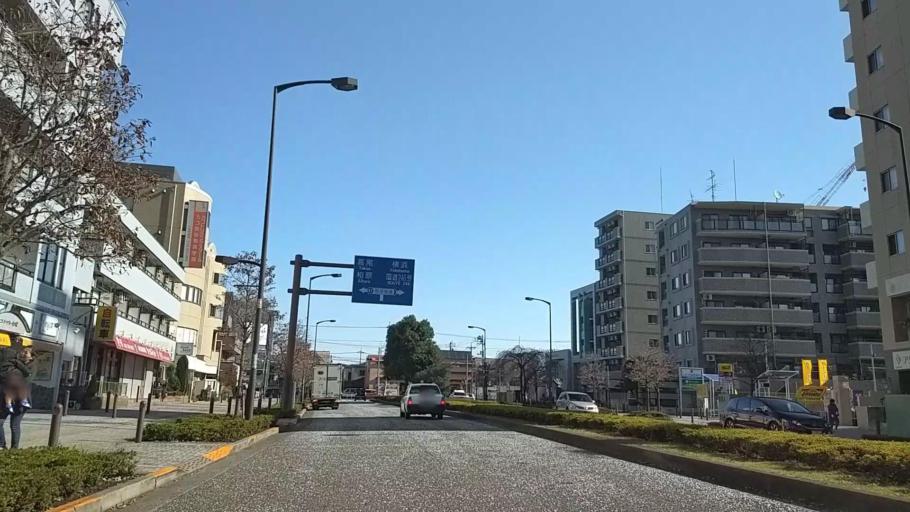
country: JP
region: Tokyo
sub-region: Machida-shi
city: Machida
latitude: 35.5446
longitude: 139.4495
